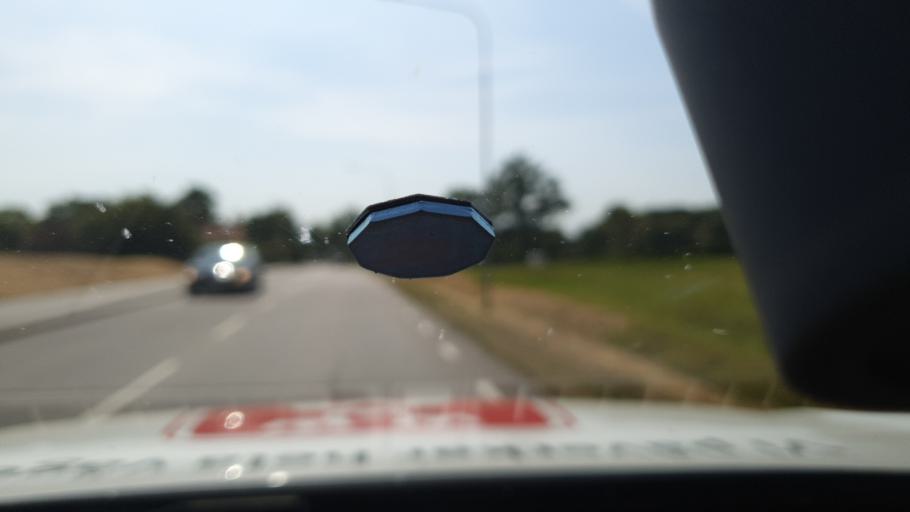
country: SE
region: Skane
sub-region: Svedala Kommun
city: Svedala
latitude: 55.5152
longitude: 13.2223
